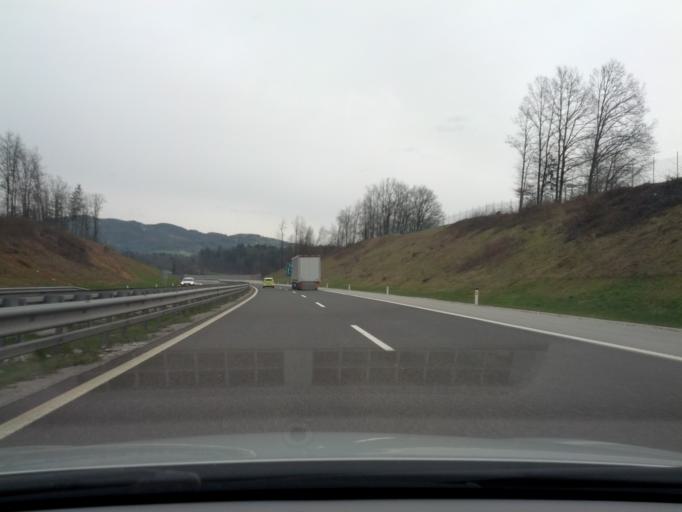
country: SI
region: Trebnje
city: Trebnje
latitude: 45.8985
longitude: 15.0345
